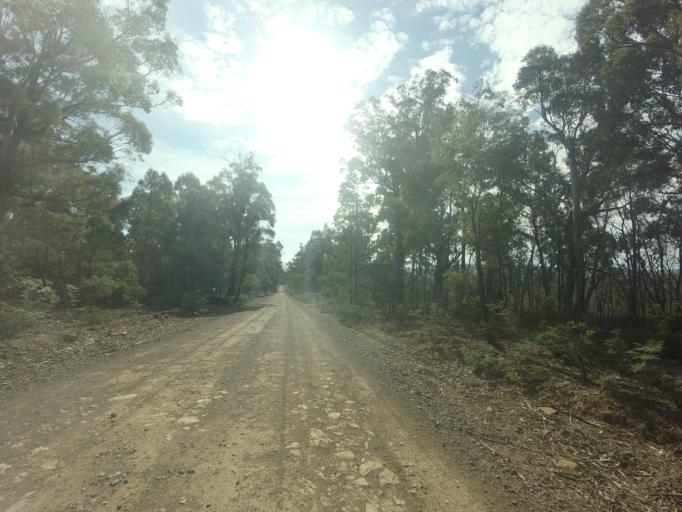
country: AU
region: Tasmania
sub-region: Sorell
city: Sorell
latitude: -42.5486
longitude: 147.4584
